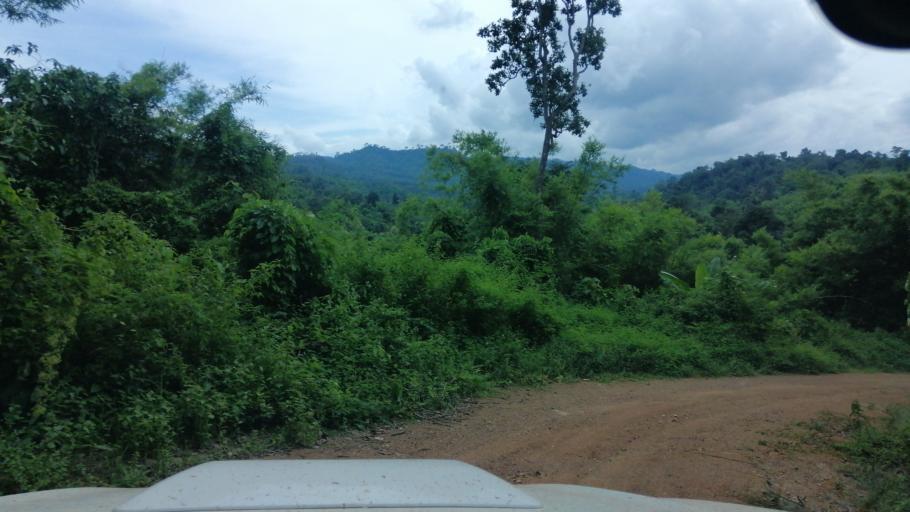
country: TH
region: Nan
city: Mae Charim
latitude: 18.7503
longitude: 101.2902
